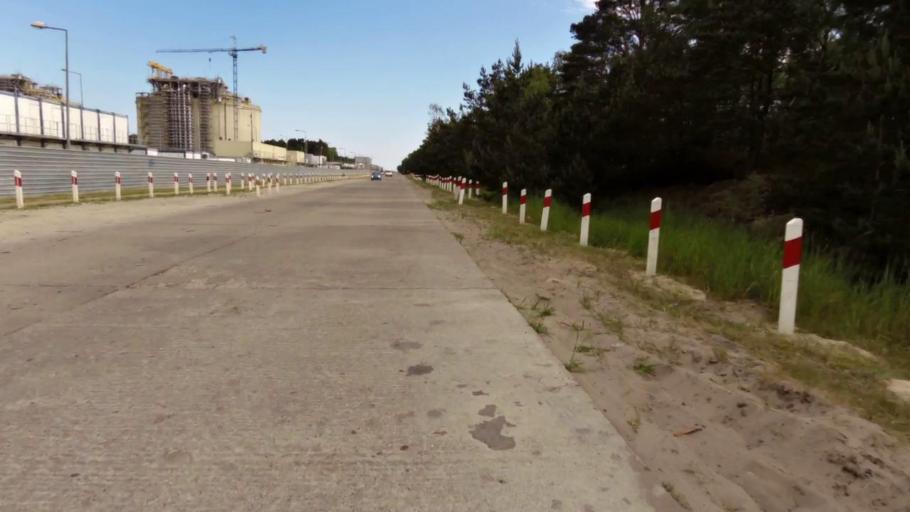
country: PL
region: West Pomeranian Voivodeship
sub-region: Swinoujscie
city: Swinoujscie
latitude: 53.9072
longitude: 14.2984
